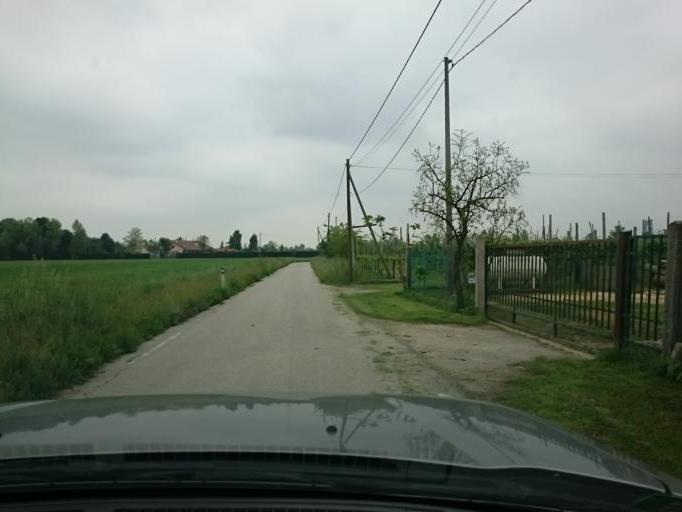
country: IT
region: Veneto
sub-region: Provincia di Padova
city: Cartura
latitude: 45.2915
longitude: 11.8591
